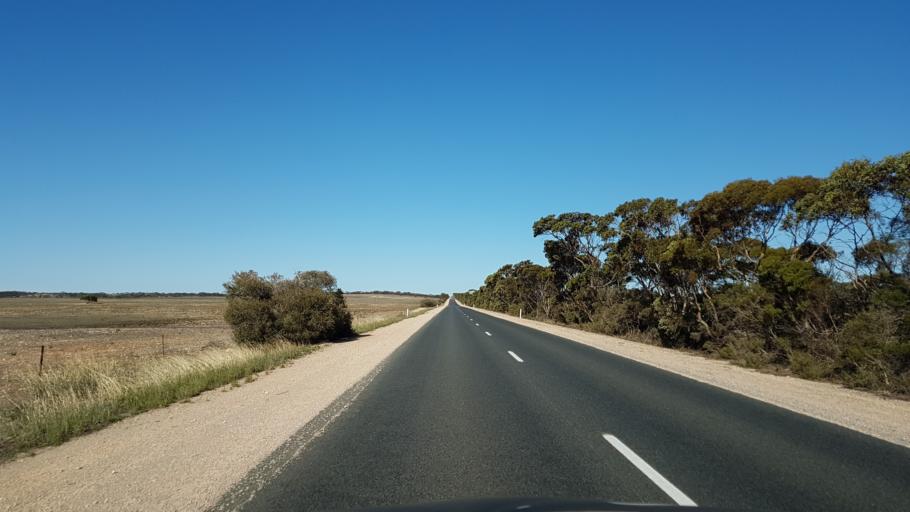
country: AU
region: South Australia
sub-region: Mid Murray
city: Mannum
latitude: -34.7571
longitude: 139.5032
